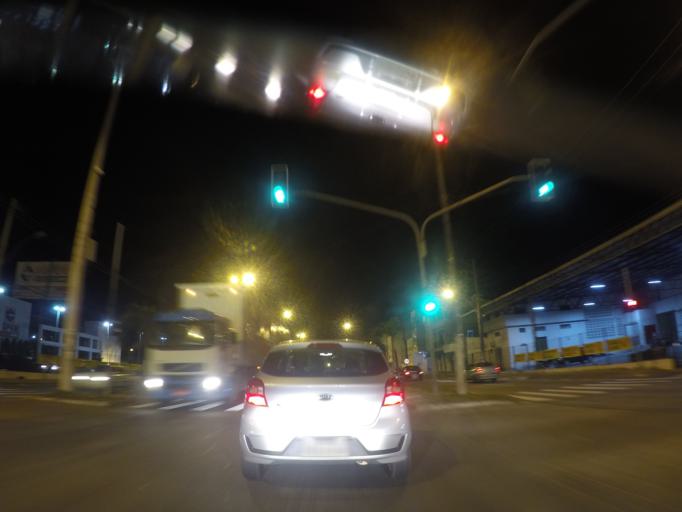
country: BR
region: Espirito Santo
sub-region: Linhares
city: Linhares
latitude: -19.3997
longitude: -40.0624
